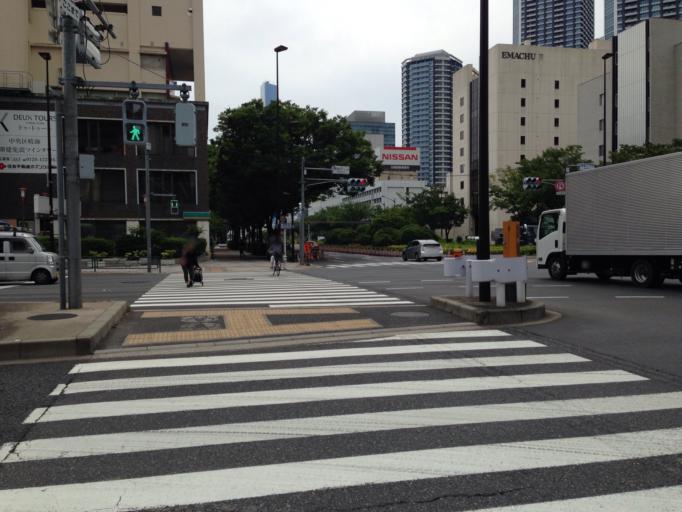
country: JP
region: Tokyo
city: Tokyo
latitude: 35.6553
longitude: 139.7820
